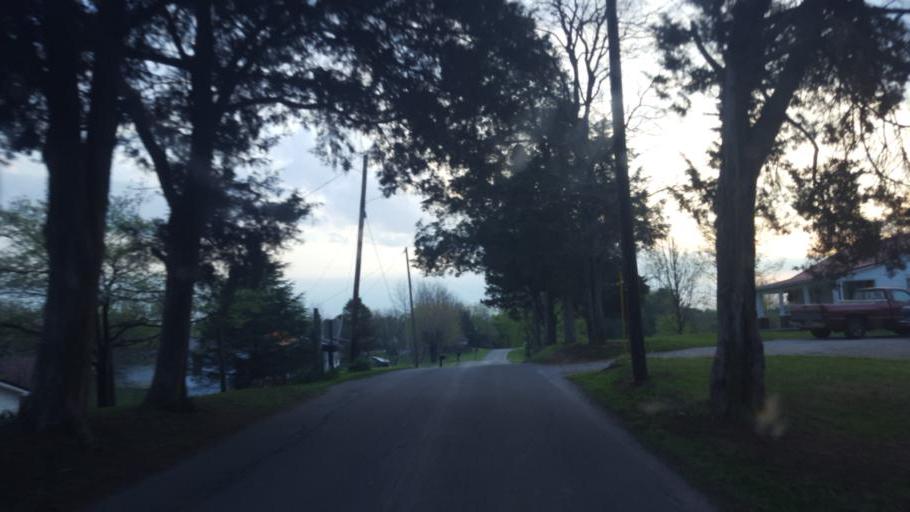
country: US
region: Kentucky
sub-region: Hart County
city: Munfordville
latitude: 37.2773
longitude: -85.9016
